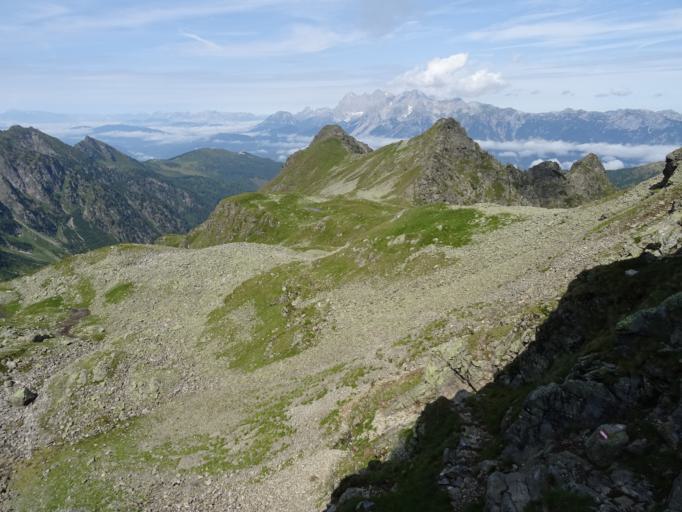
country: AT
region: Styria
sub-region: Politischer Bezirk Liezen
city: Haus
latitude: 47.3477
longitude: 13.7888
